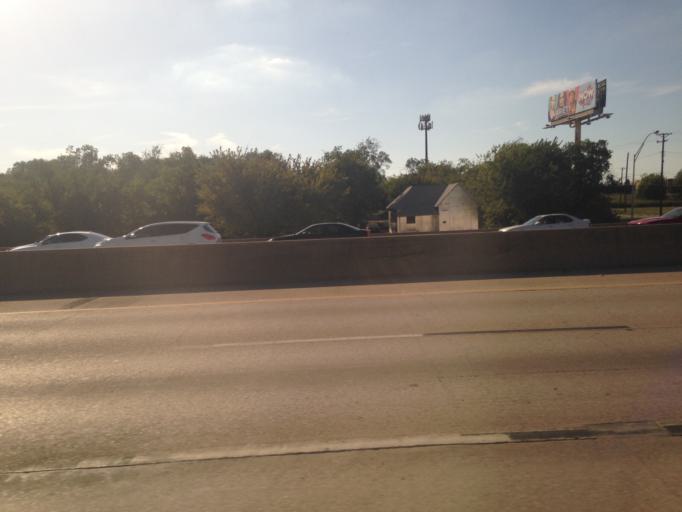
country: US
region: Texas
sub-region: Tarrant County
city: Fort Worth
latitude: 32.7287
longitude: -97.3203
